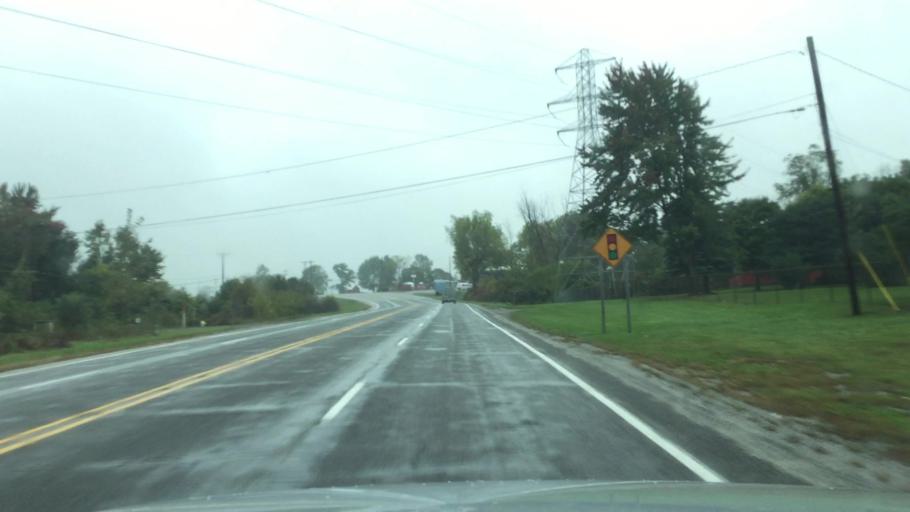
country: US
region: Michigan
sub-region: Saginaw County
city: Bridgeport
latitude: 43.3323
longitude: -83.8314
